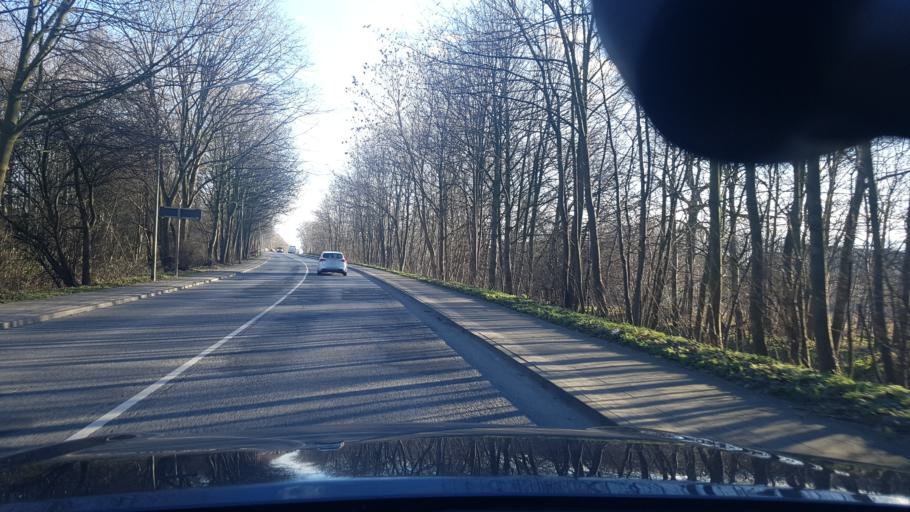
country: DE
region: Lower Saxony
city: Langen
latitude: 53.5919
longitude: 8.5487
